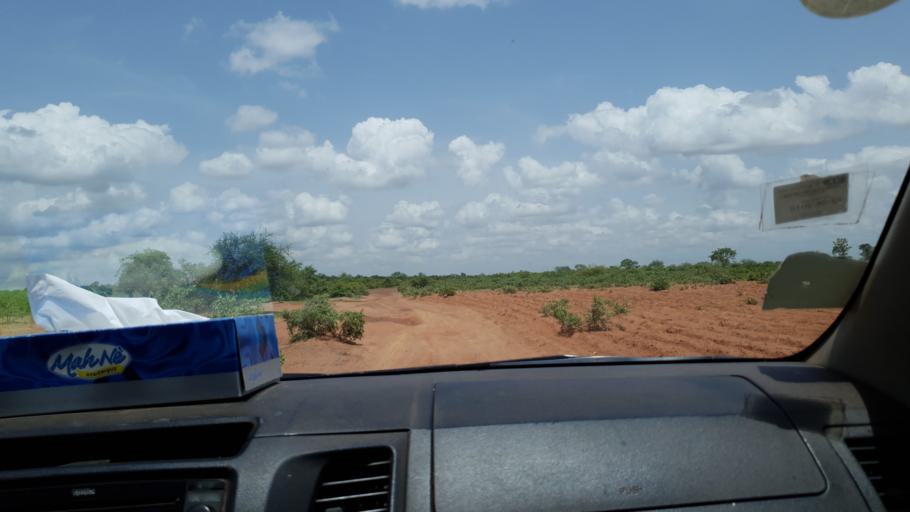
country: ML
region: Koulikoro
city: Banamba
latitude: 13.3787
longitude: -7.2066
